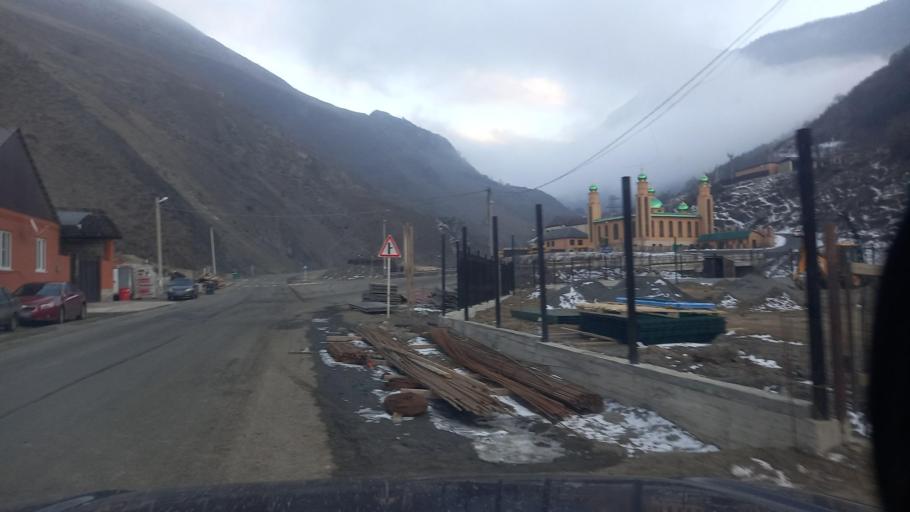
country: RU
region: Ingushetiya
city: Dzhayrakh
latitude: 42.8021
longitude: 44.7553
